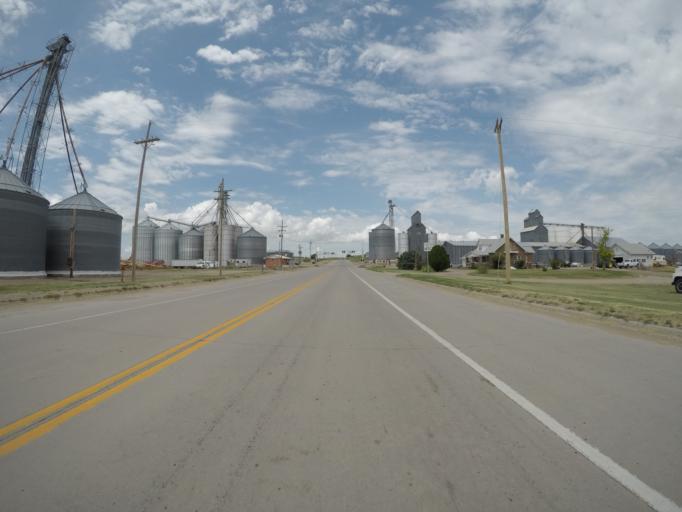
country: US
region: Kansas
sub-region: Rawlins County
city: Atwood
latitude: 39.8221
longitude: -101.0468
